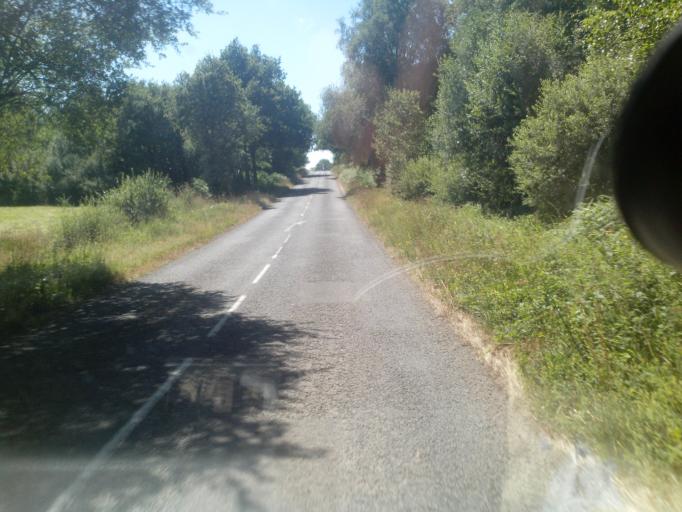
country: FR
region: Brittany
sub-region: Departement du Morbihan
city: Campeneac
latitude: 48.0000
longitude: -2.2425
